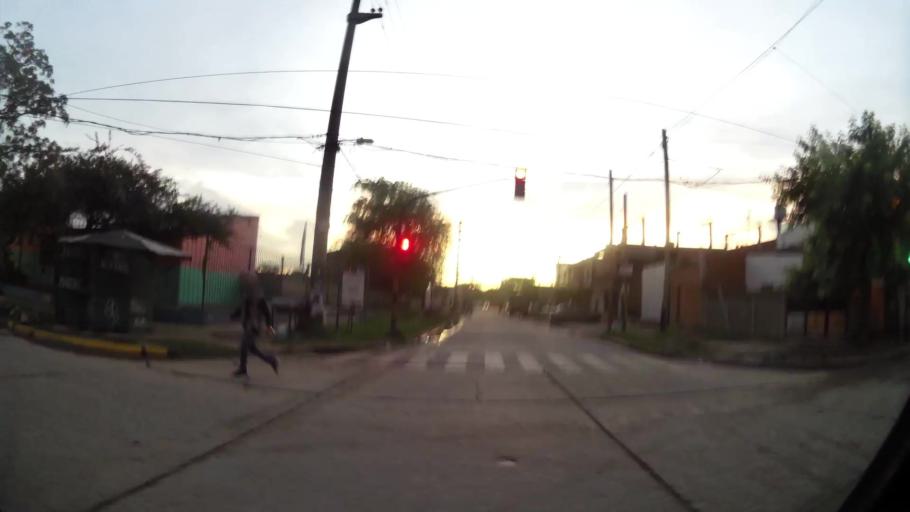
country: AR
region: Buenos Aires
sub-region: Partido de Lomas de Zamora
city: Lomas de Zamora
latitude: -34.7455
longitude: -58.3668
